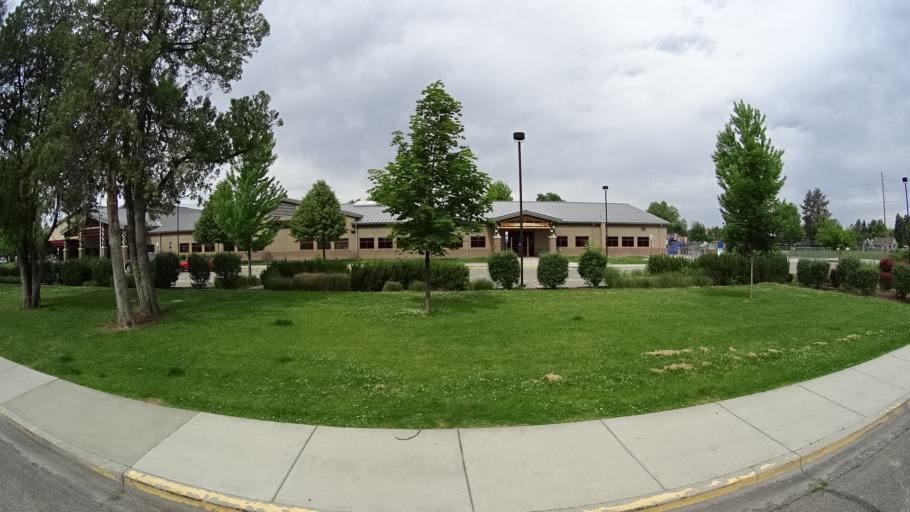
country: US
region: Idaho
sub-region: Ada County
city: Boise
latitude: 43.5884
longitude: -116.2237
